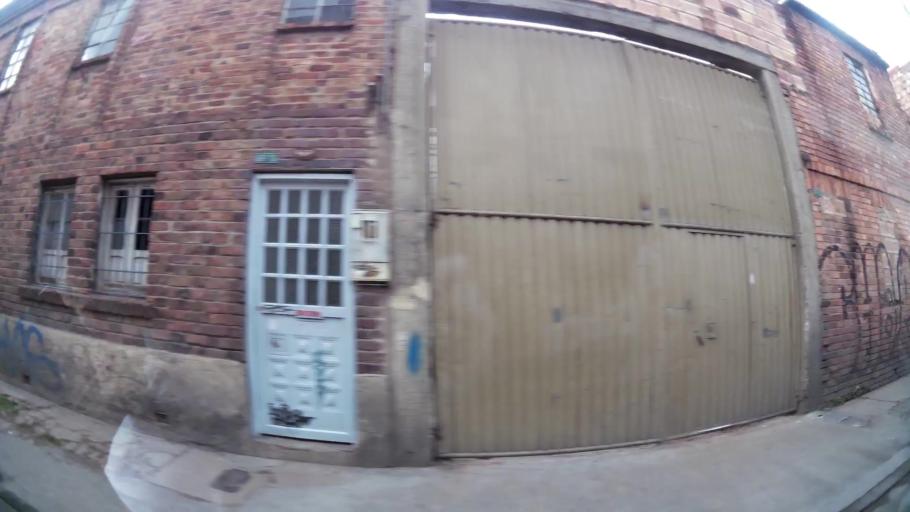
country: CO
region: Bogota D.C.
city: Barrio San Luis
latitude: 4.6868
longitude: -74.0876
